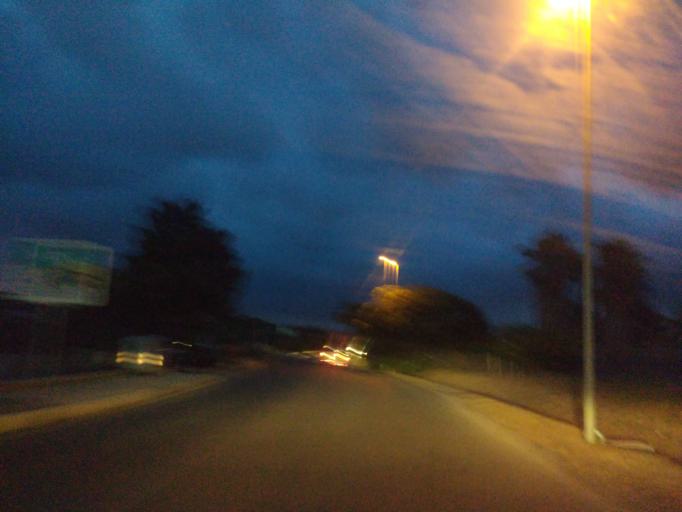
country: IT
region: Latium
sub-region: Citta metropolitana di Roma Capitale
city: Anzio
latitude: 41.4547
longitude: 12.6224
